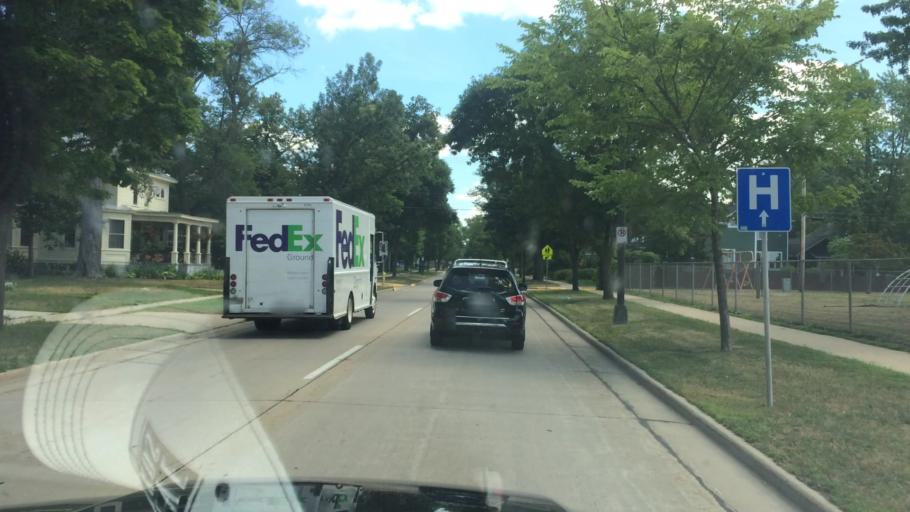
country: US
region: Wisconsin
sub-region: Portage County
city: Stevens Point
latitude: 44.5223
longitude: -89.5706
